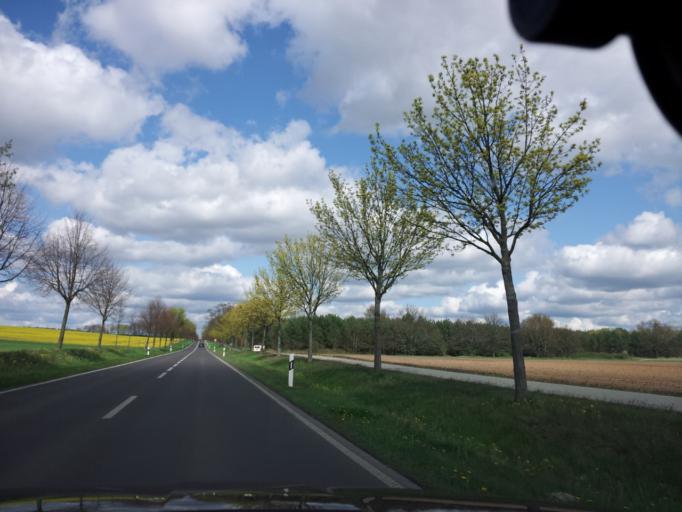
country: DE
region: Brandenburg
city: Bernau bei Berlin
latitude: 52.6924
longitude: 13.6034
